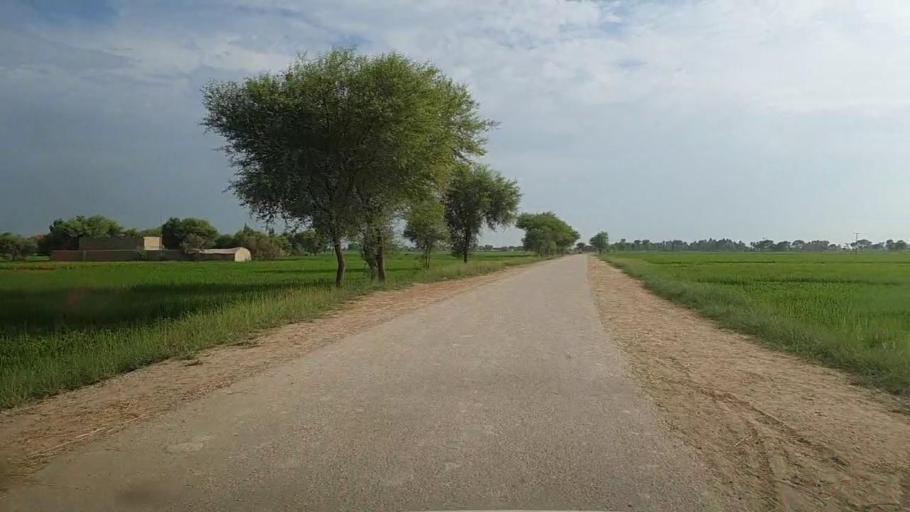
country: PK
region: Sindh
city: Thul
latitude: 28.2638
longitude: 68.8595
